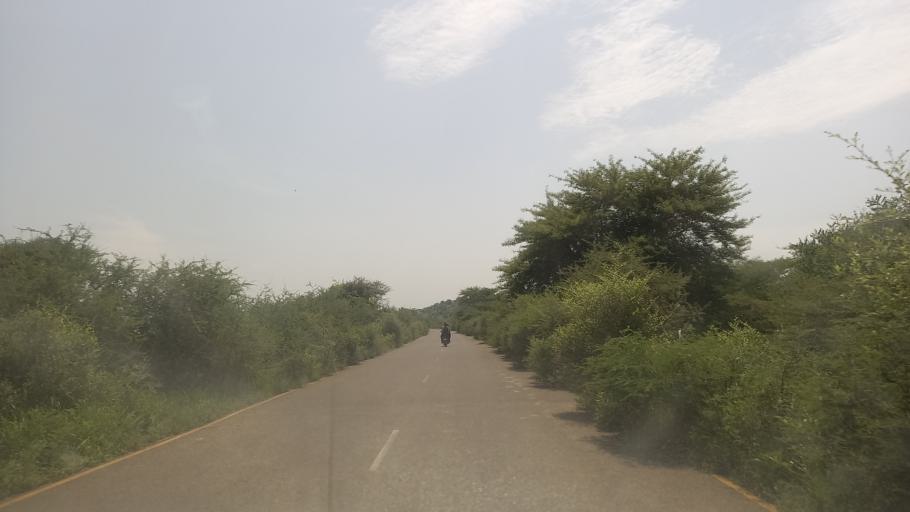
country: ET
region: Gambela
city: Gambela
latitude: 8.2822
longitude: 34.2209
